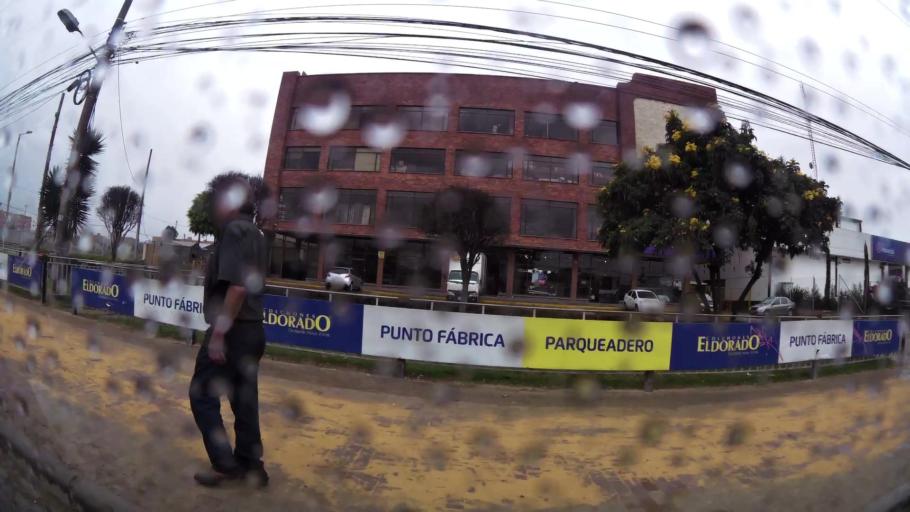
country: CO
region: Bogota D.C.
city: Bogota
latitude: 4.6568
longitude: -74.1335
